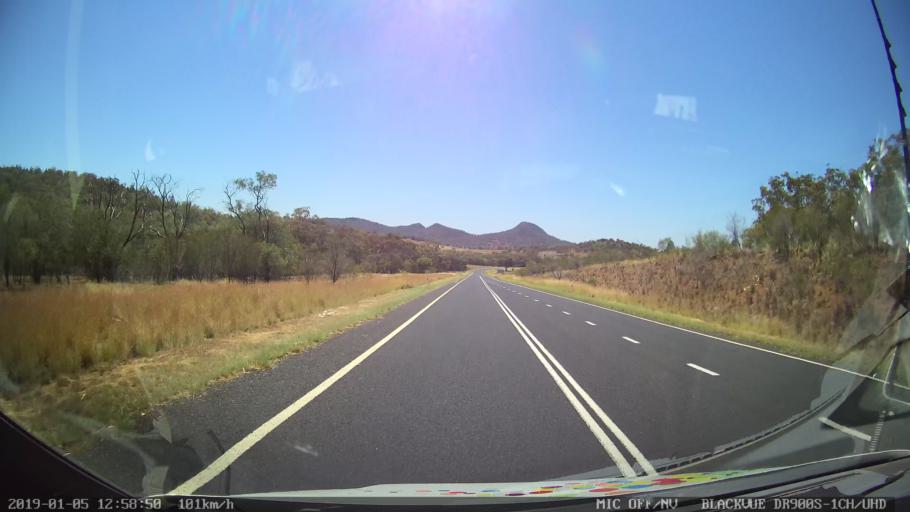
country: AU
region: New South Wales
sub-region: Narrabri
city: Boggabri
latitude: -31.1133
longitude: 149.7561
